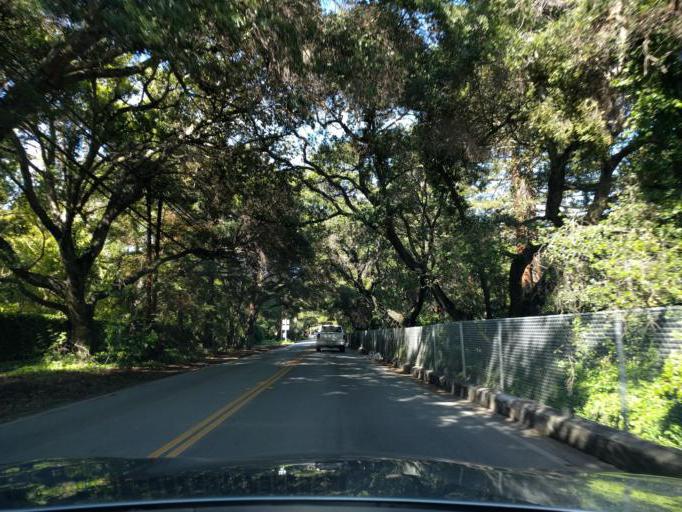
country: US
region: California
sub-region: San Mateo County
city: North Fair Oaks
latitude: 37.4695
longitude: -122.1910
